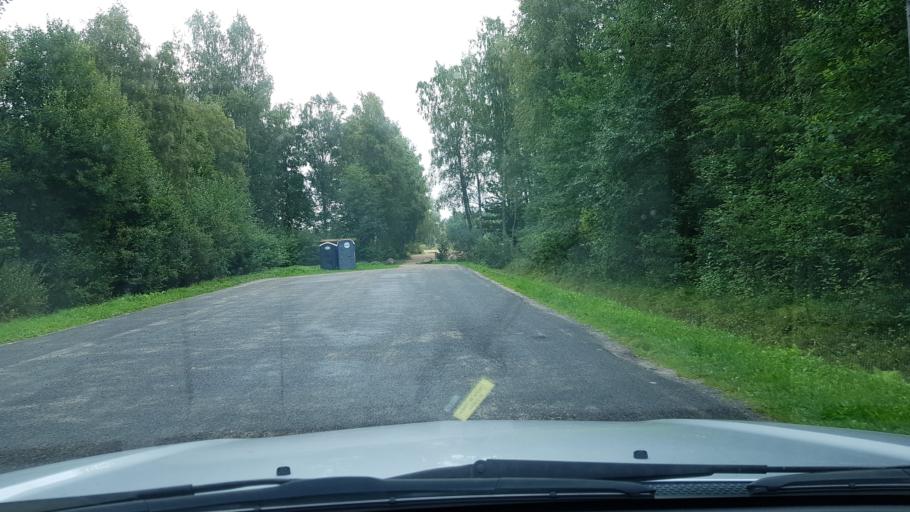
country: EE
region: Harju
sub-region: Rae vald
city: Jueri
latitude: 59.3544
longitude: 24.9380
